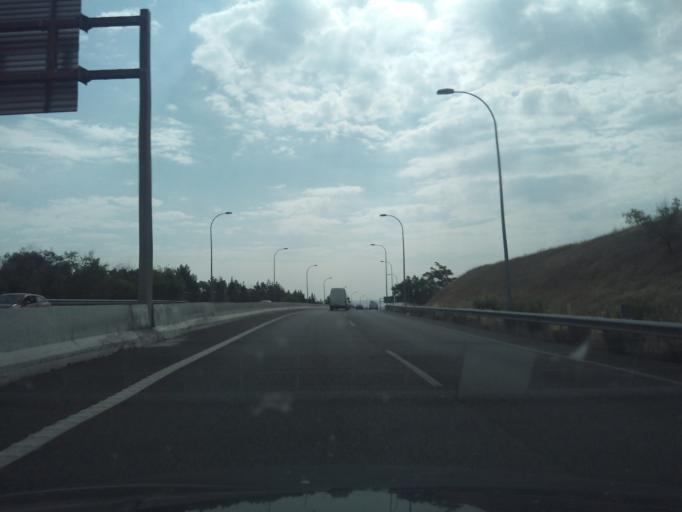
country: ES
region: Madrid
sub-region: Provincia de Madrid
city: Coslada
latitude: 40.4406
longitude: -3.5798
